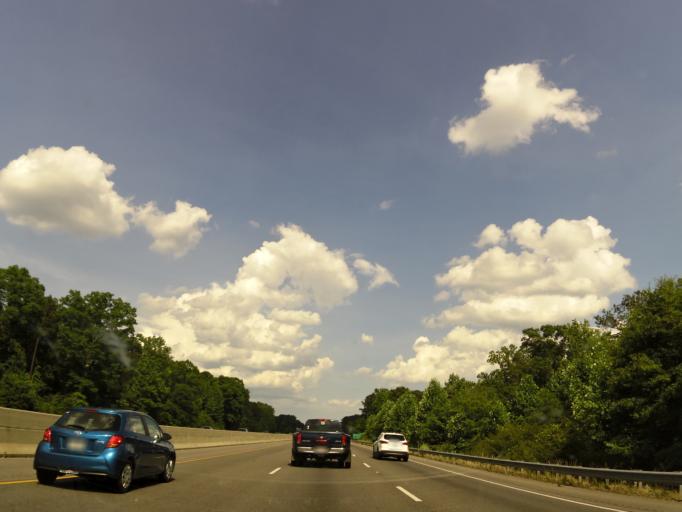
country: US
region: Alabama
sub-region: Tuscaloosa County
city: Coaling
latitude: 33.1897
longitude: -87.3094
